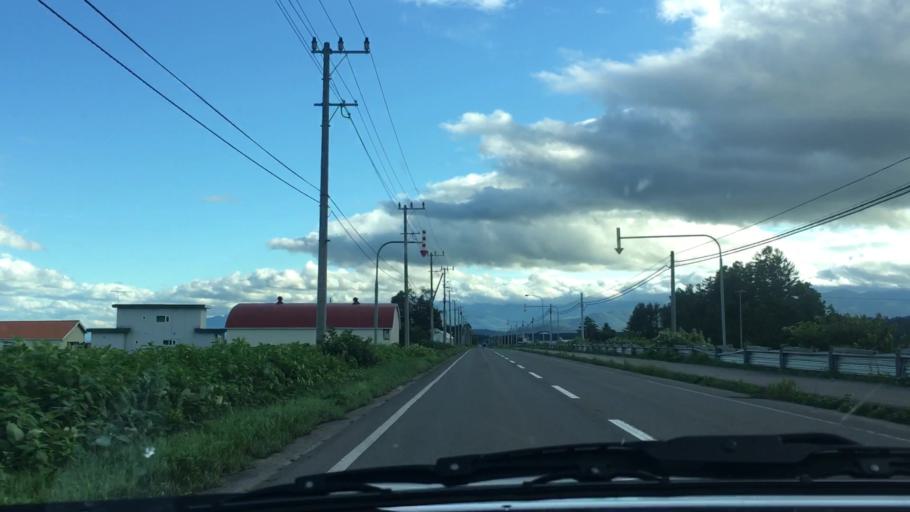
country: JP
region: Hokkaido
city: Otofuke
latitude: 43.1500
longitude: 142.8998
